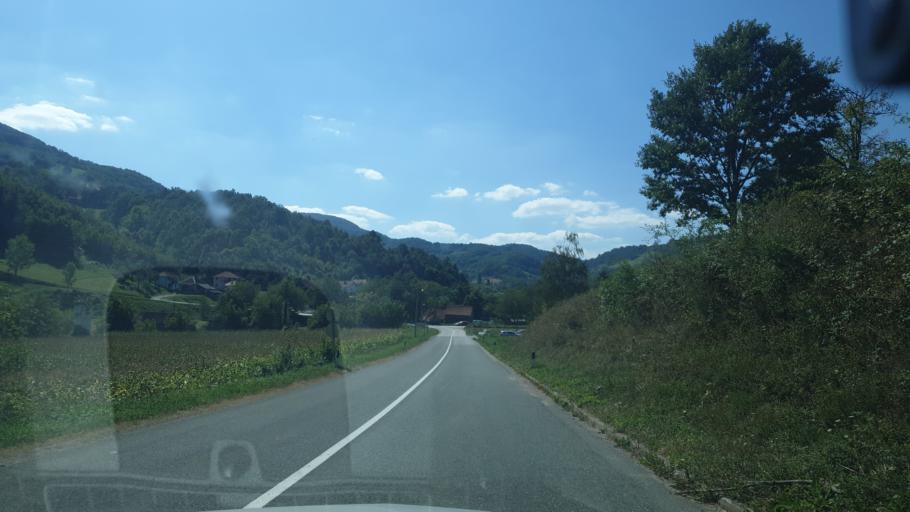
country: RS
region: Central Serbia
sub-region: Kolubarski Okrug
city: Mionica
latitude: 44.1619
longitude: 19.9865
